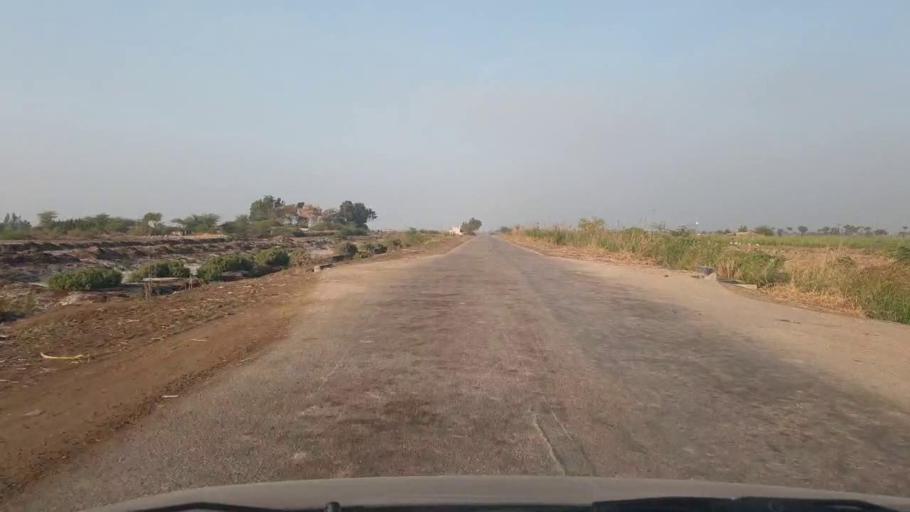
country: PK
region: Sindh
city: Mirwah Gorchani
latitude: 25.3452
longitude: 69.1709
